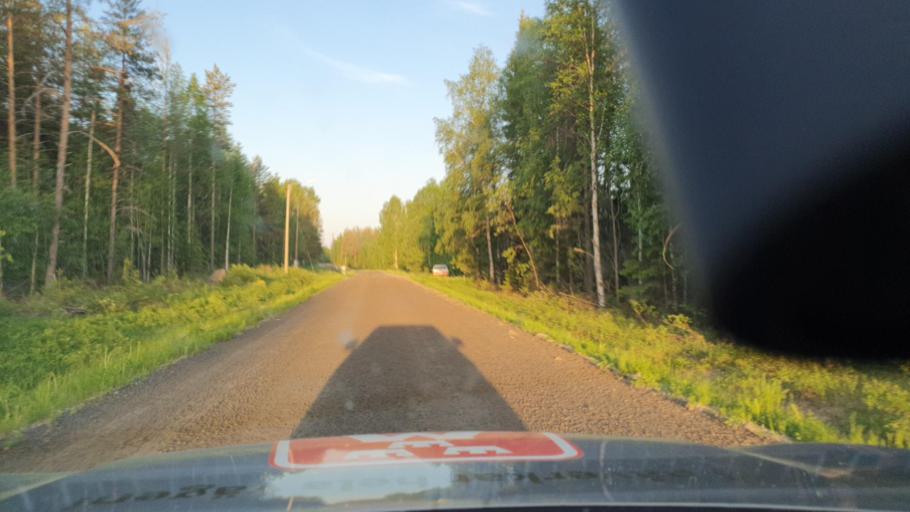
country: SE
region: Norrbotten
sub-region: Bodens Kommun
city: Boden
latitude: 66.0558
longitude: 21.7429
